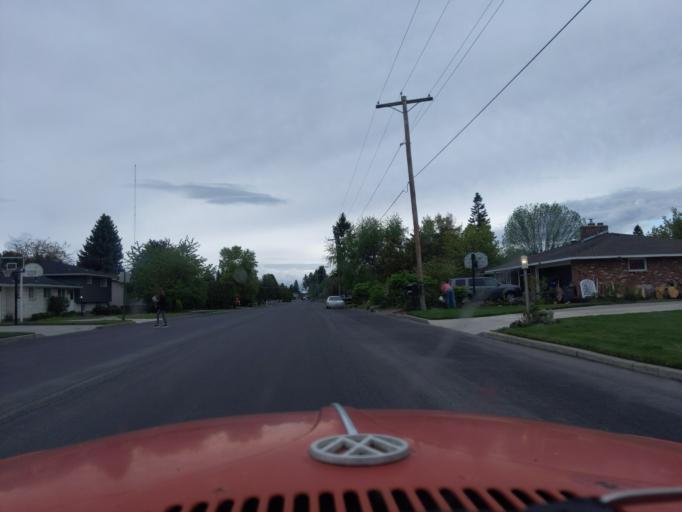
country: US
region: Washington
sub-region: Spokane County
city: Spokane
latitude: 47.6014
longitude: -117.3792
